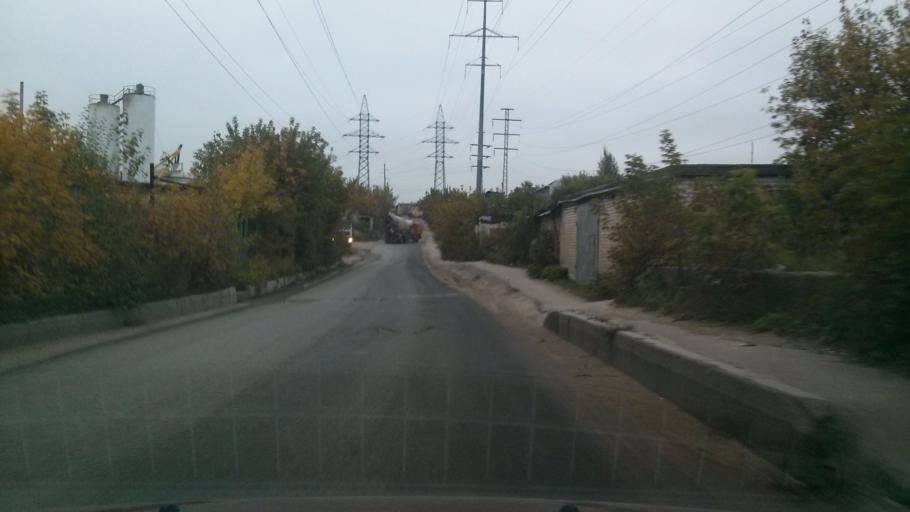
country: RU
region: Nizjnij Novgorod
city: Nizhniy Novgorod
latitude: 56.3063
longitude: 44.0097
